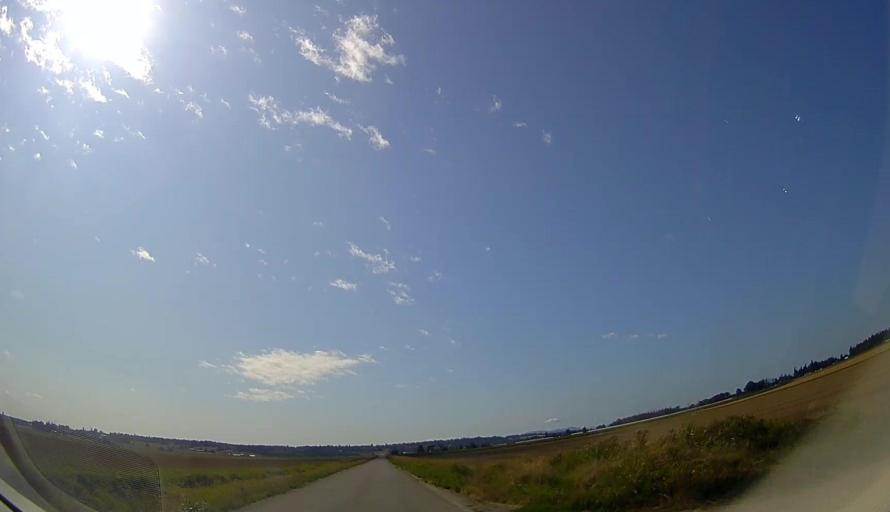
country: US
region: Washington
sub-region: Skagit County
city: Burlington
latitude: 48.4938
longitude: -122.3676
